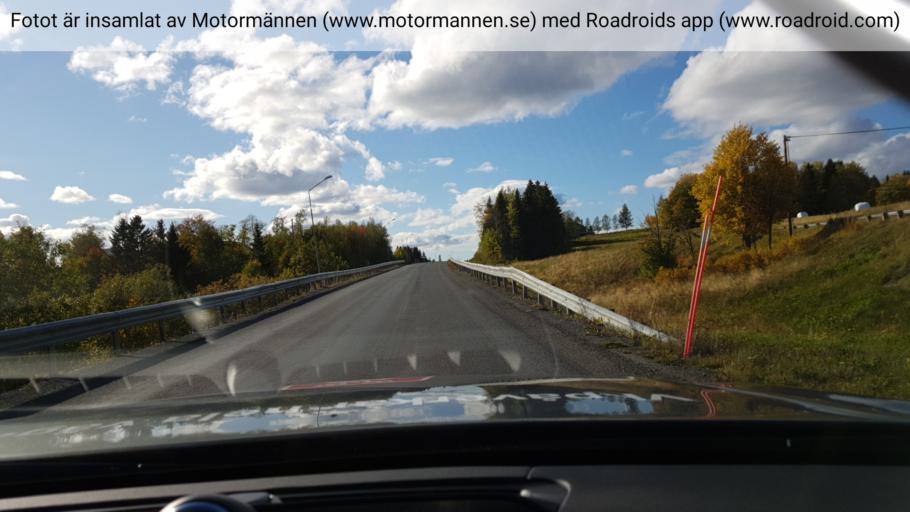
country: SE
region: Jaemtland
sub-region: Krokoms Kommun
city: Valla
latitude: 63.1849
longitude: 14.0340
